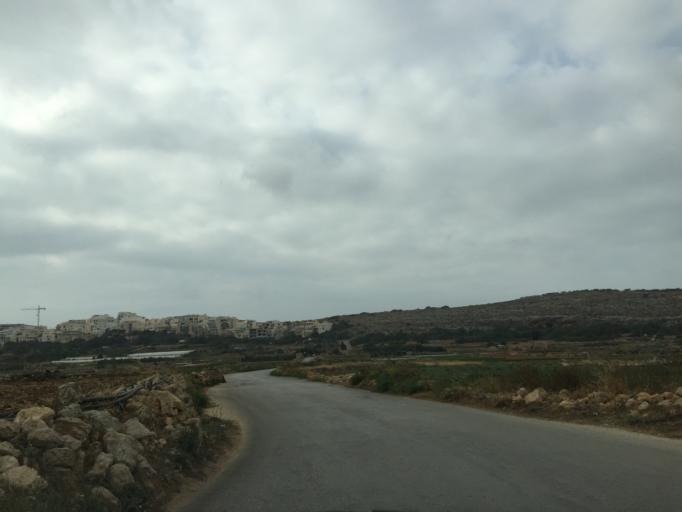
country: MT
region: L-Imgarr
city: Imgarr
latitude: 35.9350
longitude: 14.3591
